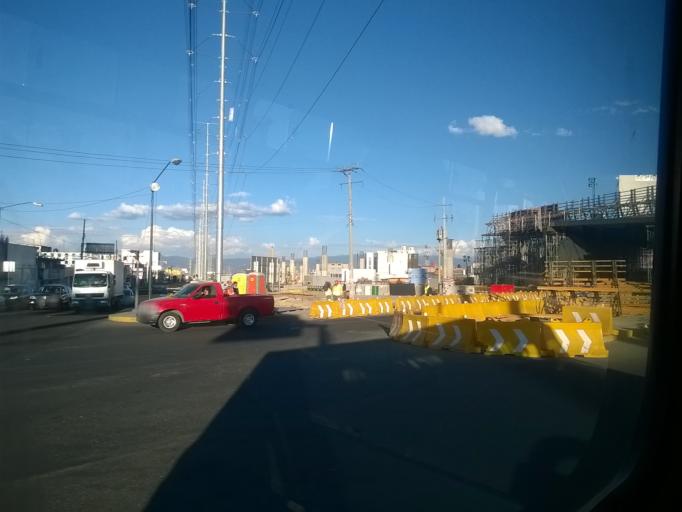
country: MX
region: Mexico
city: Toluca
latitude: 19.2708
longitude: -99.6418
